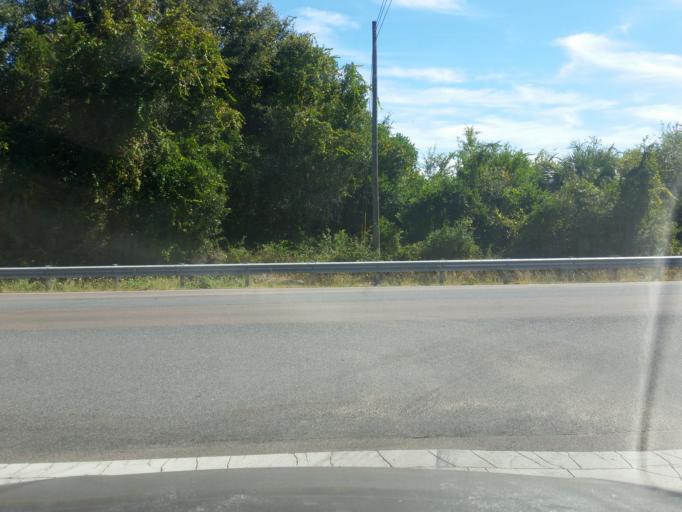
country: US
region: Florida
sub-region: Escambia County
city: East Pensacola Heights
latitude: 30.4582
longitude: -87.1674
